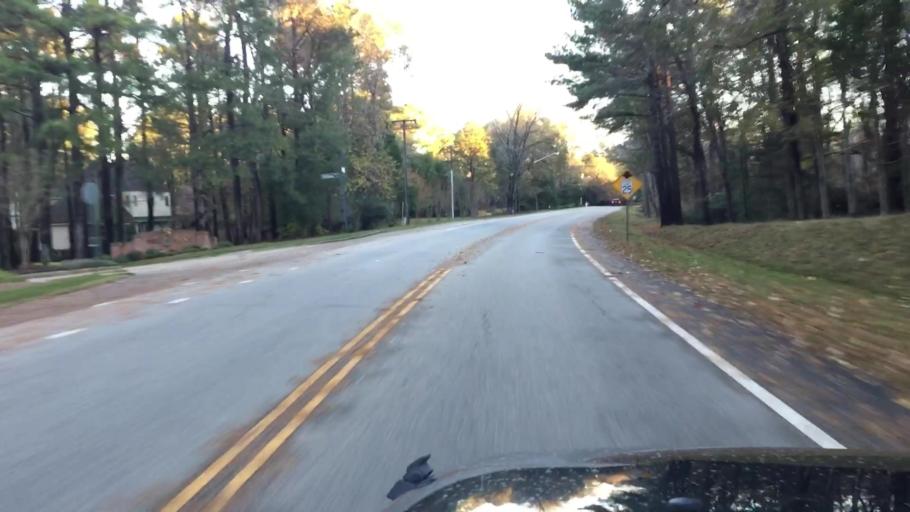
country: US
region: Virginia
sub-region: City of Williamsburg
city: Williamsburg
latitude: 37.2574
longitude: -76.7104
